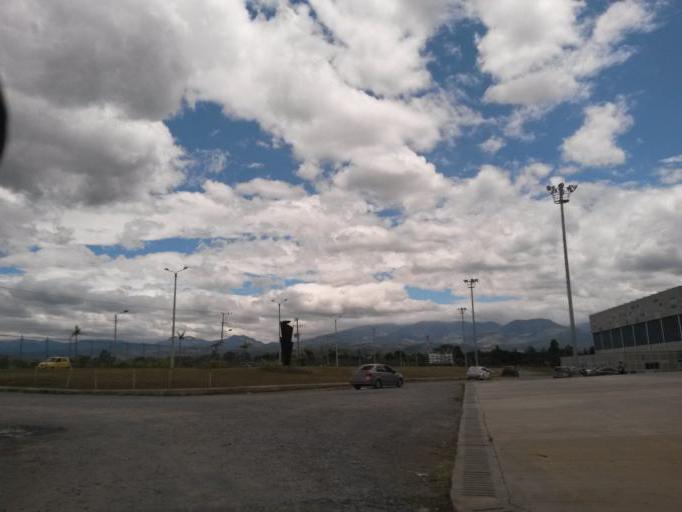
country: CO
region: Cauca
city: Popayan
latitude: 2.4903
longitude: -76.5929
